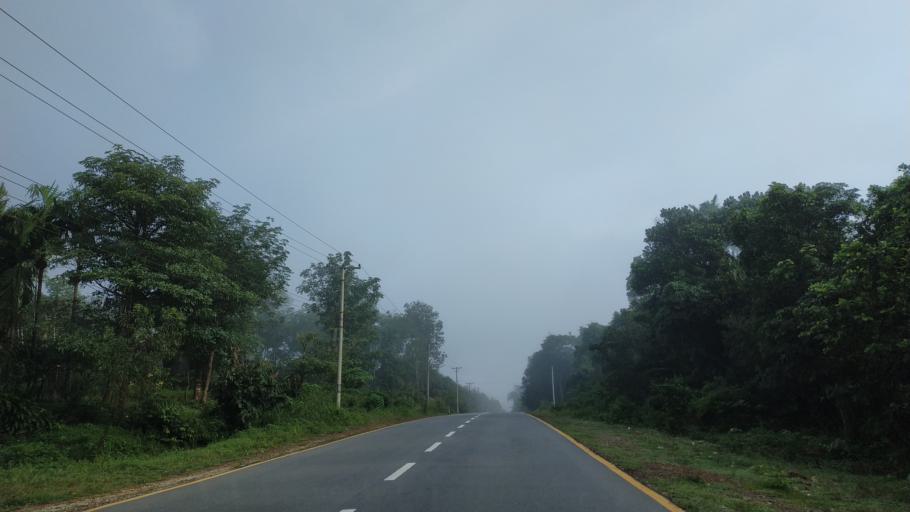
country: MM
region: Tanintharyi
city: Dawei
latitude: 14.2133
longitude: 98.2090
